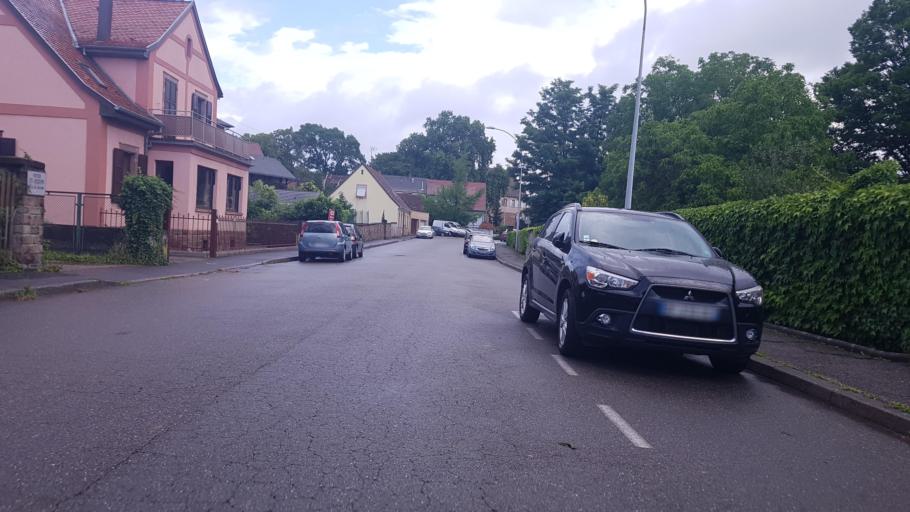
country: FR
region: Alsace
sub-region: Departement du Bas-Rhin
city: Saverne
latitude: 48.7379
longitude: 7.3637
